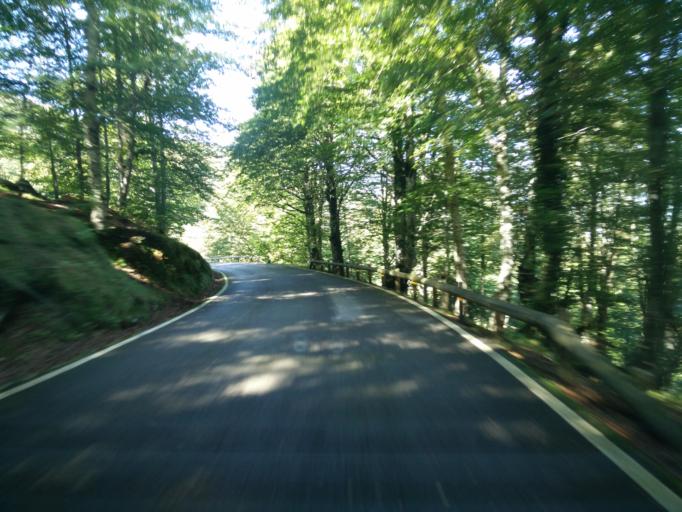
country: ES
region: Cantabria
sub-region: Provincia de Cantabria
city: Ruente
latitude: 43.1017
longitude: -4.2733
